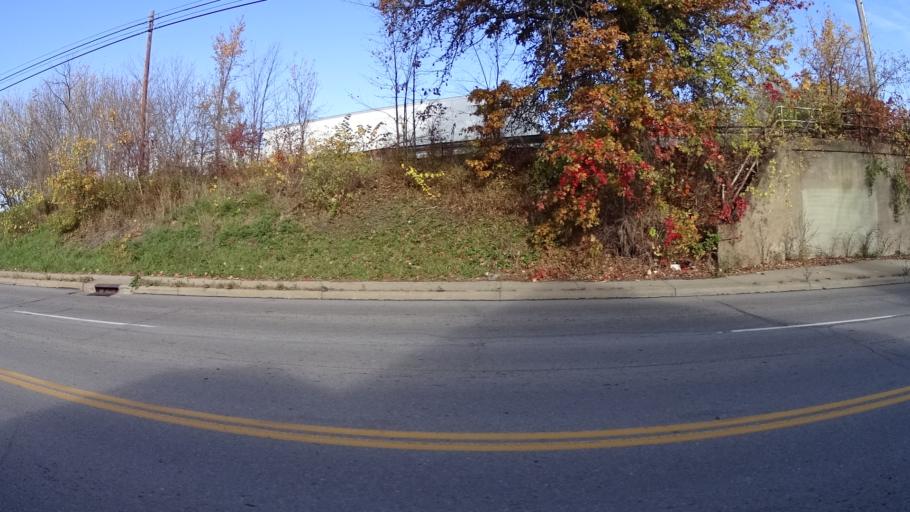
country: US
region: Ohio
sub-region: Lorain County
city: Lorain
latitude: 41.4519
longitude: -82.1629
